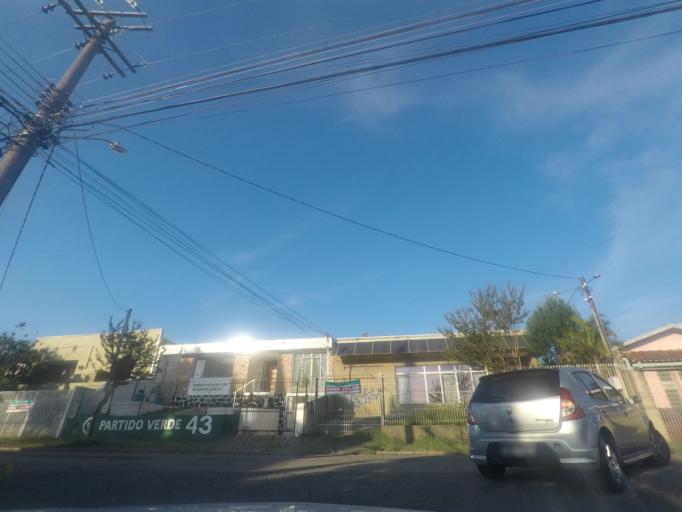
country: BR
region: Parana
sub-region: Curitiba
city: Curitiba
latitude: -25.4088
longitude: -49.2734
